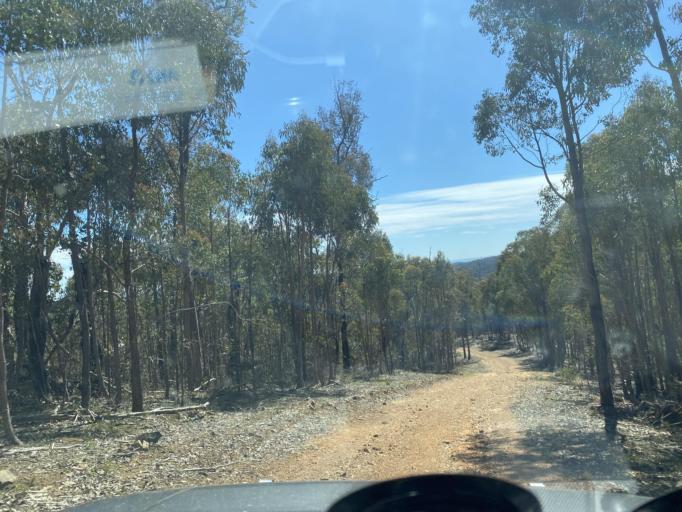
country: AU
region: Victoria
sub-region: Benalla
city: Benalla
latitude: -36.7246
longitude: 146.1807
